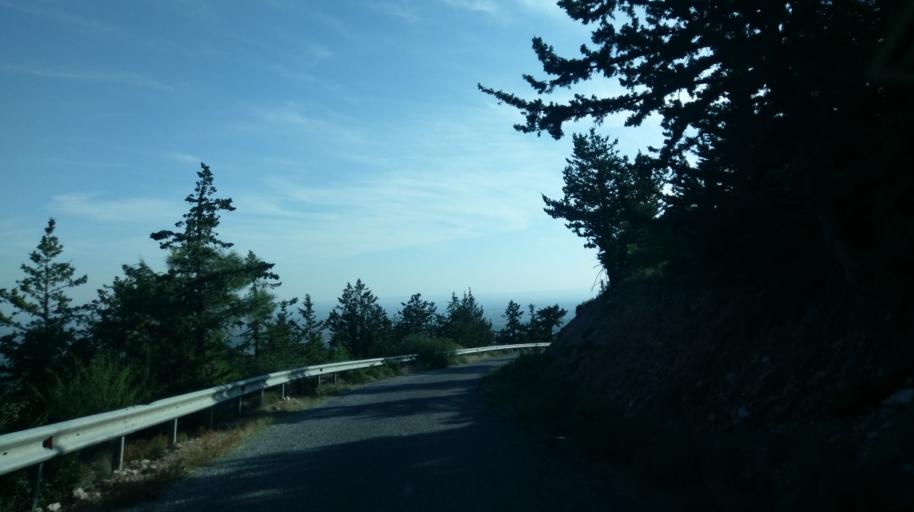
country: CY
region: Ammochostos
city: Lefkonoiko
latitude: 35.3171
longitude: 33.6193
